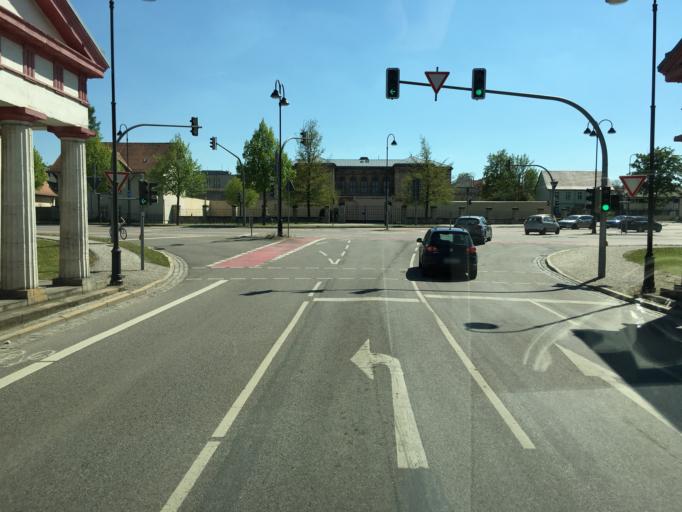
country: DE
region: Saxony-Anhalt
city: Naumburg
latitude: 51.1504
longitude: 11.8051
